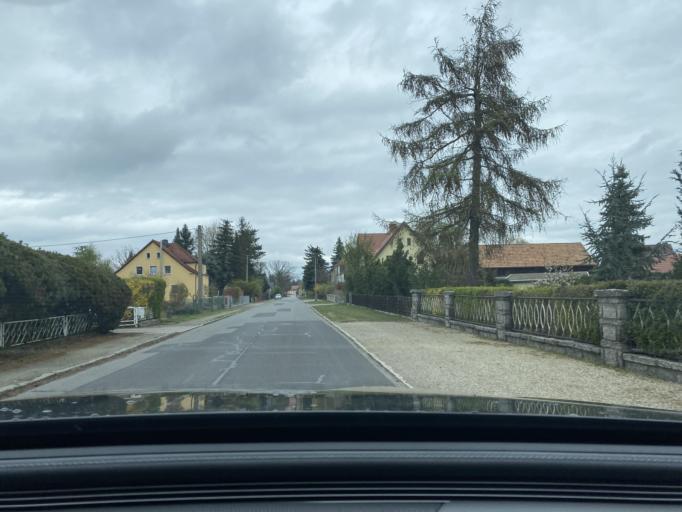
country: DE
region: Saxony
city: Neschwitz
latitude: 51.2642
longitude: 14.3301
